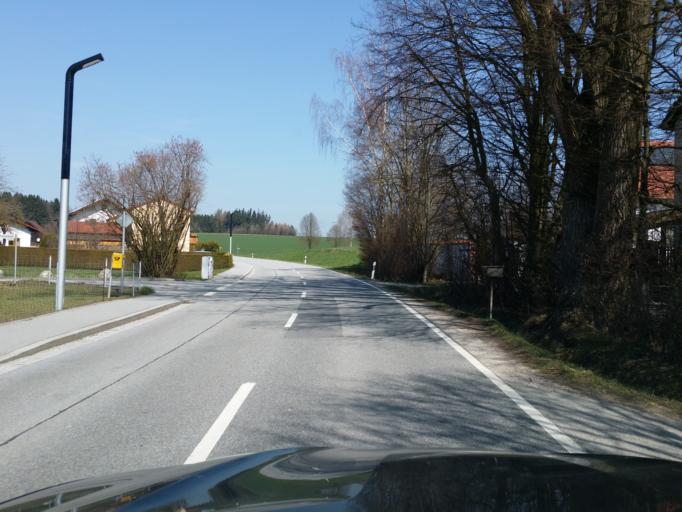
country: DE
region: Bavaria
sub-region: Upper Bavaria
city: Kirchberg
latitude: 48.4403
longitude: 12.0626
